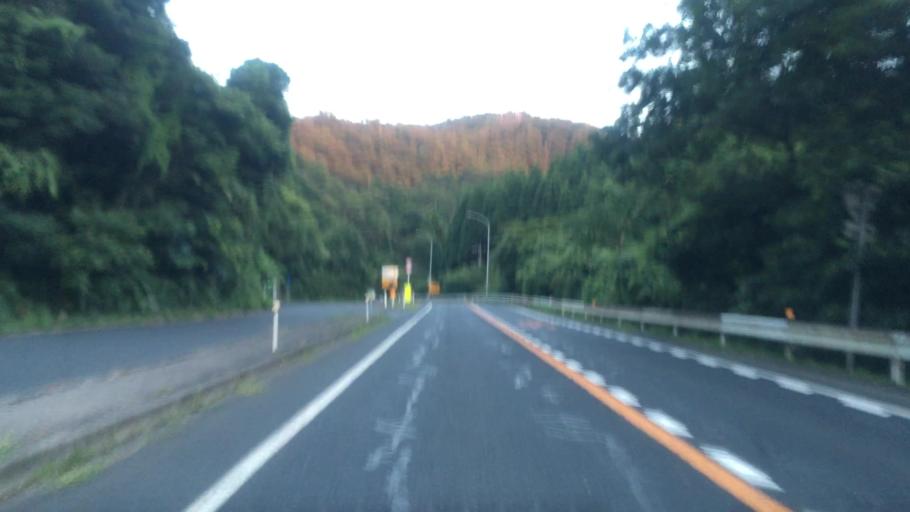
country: JP
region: Tottori
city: Tottori
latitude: 35.5950
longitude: 134.3533
